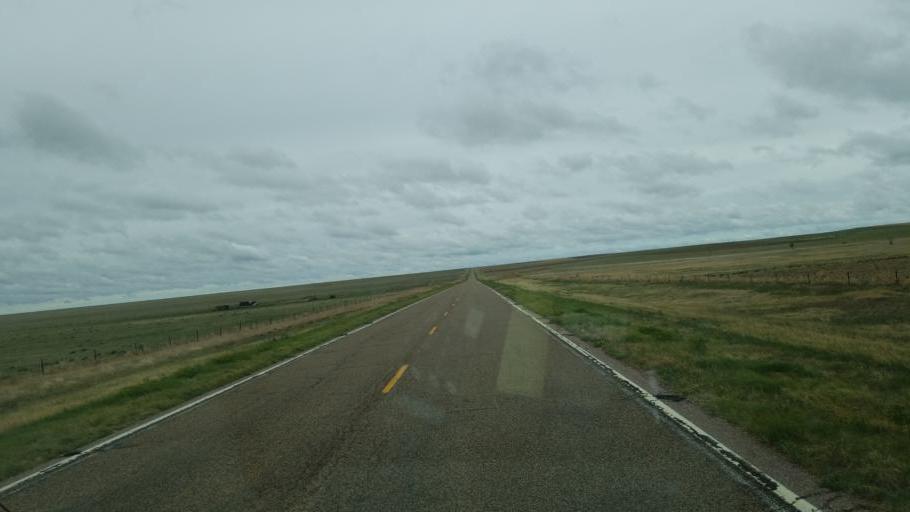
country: US
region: Colorado
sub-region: Lincoln County
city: Hugo
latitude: 38.8501
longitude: -103.4172
